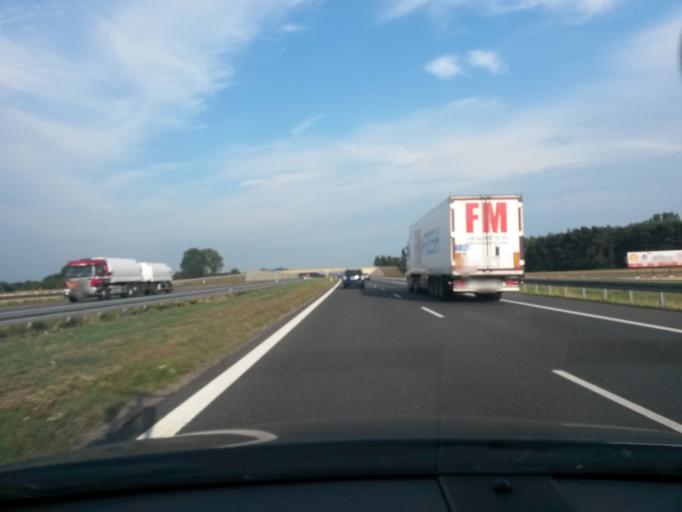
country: PL
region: Lodz Voivodeship
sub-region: Powiat zgierski
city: Parzeczew
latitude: 51.9549
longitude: 19.1403
